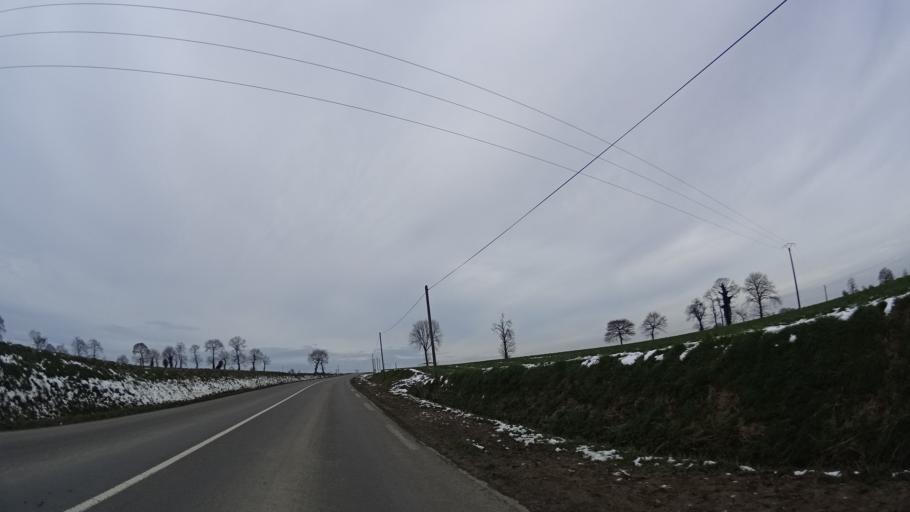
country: FR
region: Brittany
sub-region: Departement des Cotes-d'Armor
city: Plouasne
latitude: 48.3159
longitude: -1.9540
